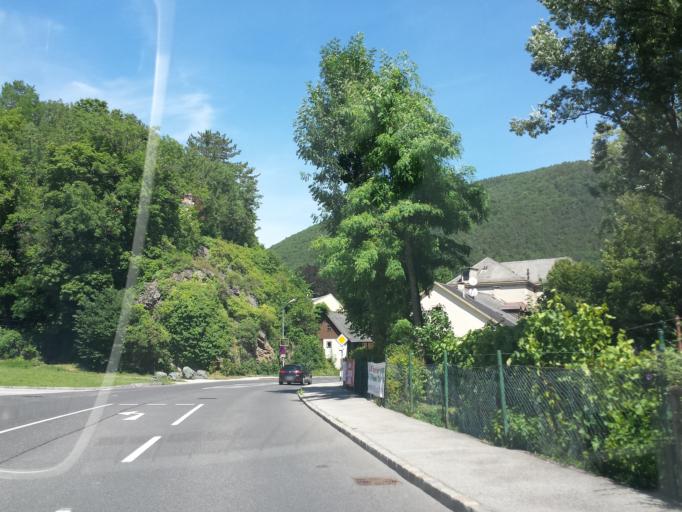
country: AT
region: Lower Austria
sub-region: Politischer Bezirk Neunkirchen
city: Gloggnitz
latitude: 47.6727
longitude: 15.9310
